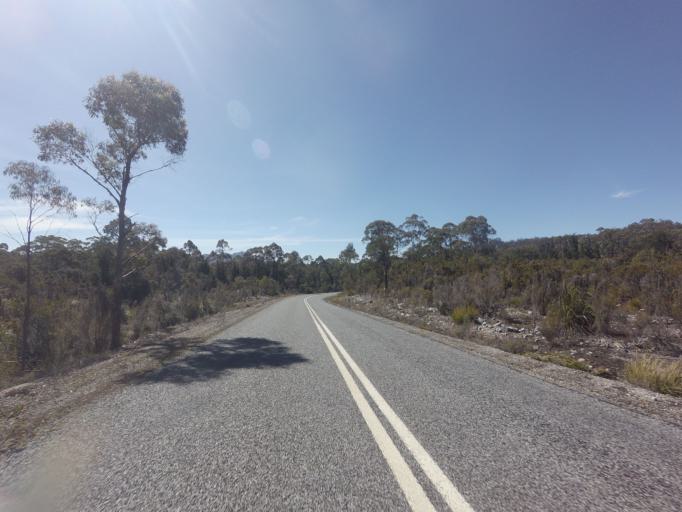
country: AU
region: Tasmania
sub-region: Huon Valley
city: Geeveston
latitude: -42.7707
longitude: 146.3967
